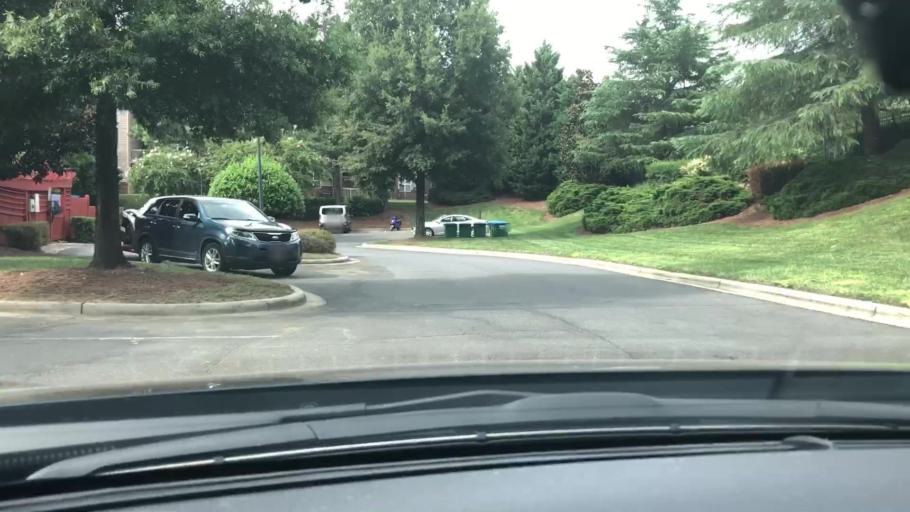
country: US
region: North Carolina
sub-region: Mecklenburg County
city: Charlotte
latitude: 35.1914
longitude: -80.8113
